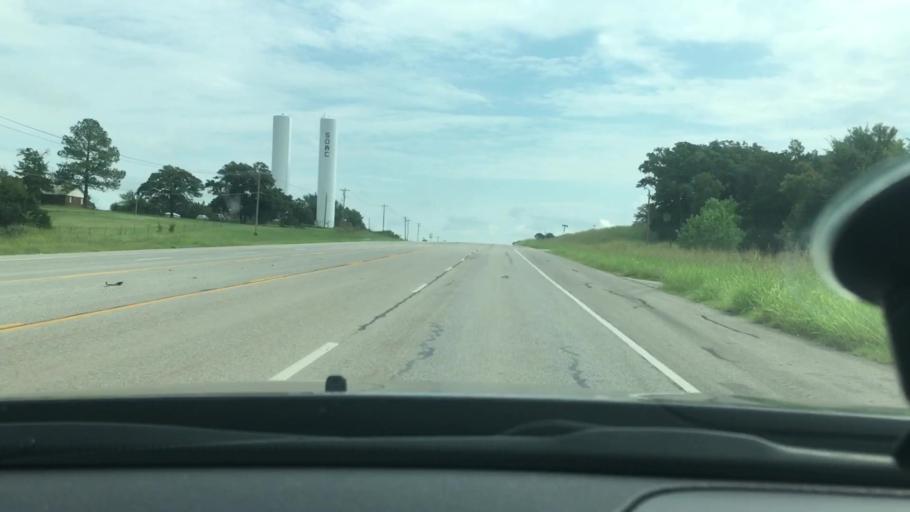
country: US
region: Oklahoma
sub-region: Carter County
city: Dickson
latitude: 34.1871
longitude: -97.0031
